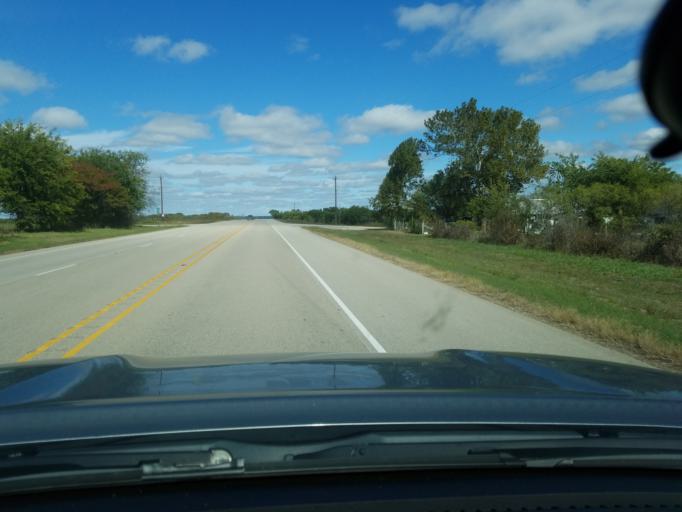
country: US
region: Texas
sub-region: Hamilton County
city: Hamilton
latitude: 31.5688
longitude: -98.1584
